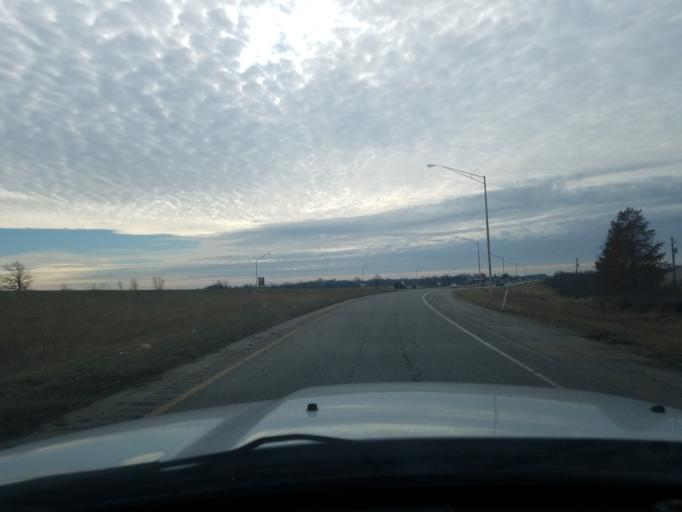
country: US
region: Indiana
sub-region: Huntington County
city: Warren
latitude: 40.7194
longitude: -85.4384
